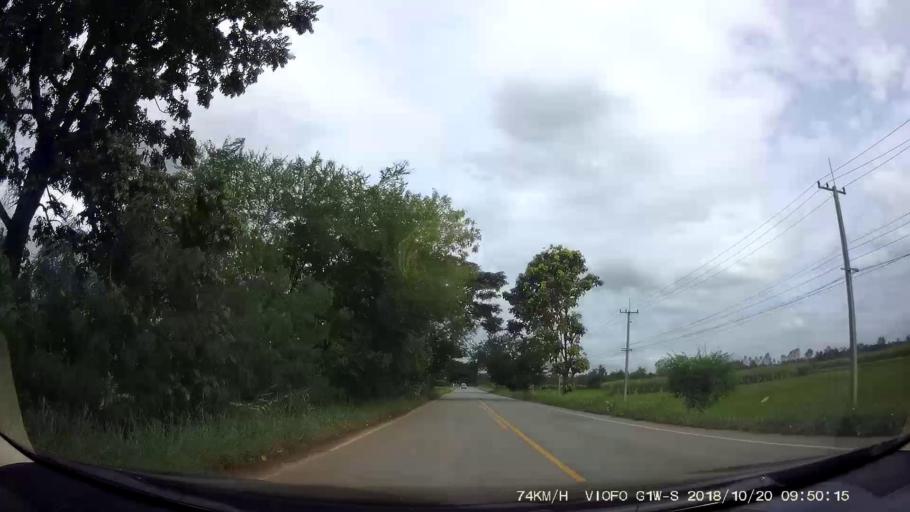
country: TH
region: Chaiyaphum
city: Khon San
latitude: 16.5290
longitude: 101.9027
